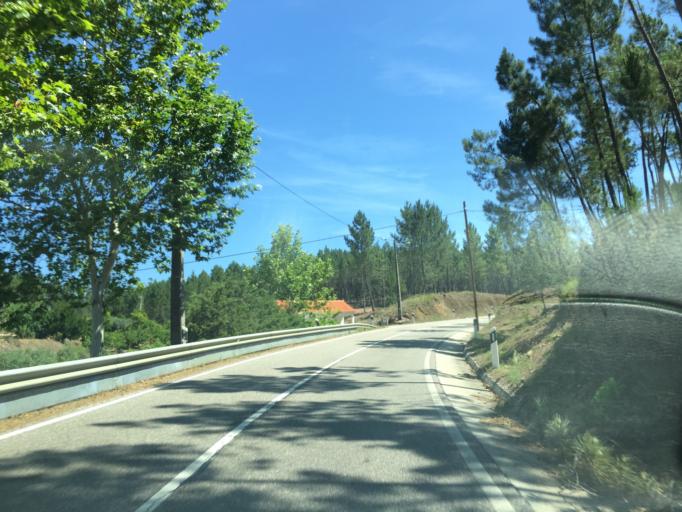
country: PT
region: Castelo Branco
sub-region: Oleiros
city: Oleiros
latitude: 39.9296
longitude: -7.8890
